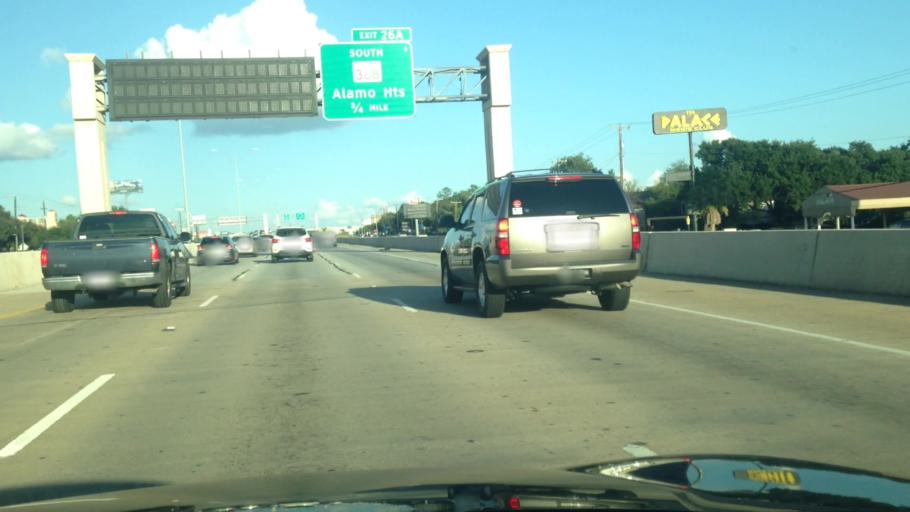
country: US
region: Texas
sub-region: Bexar County
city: Windcrest
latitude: 29.5160
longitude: -98.4176
